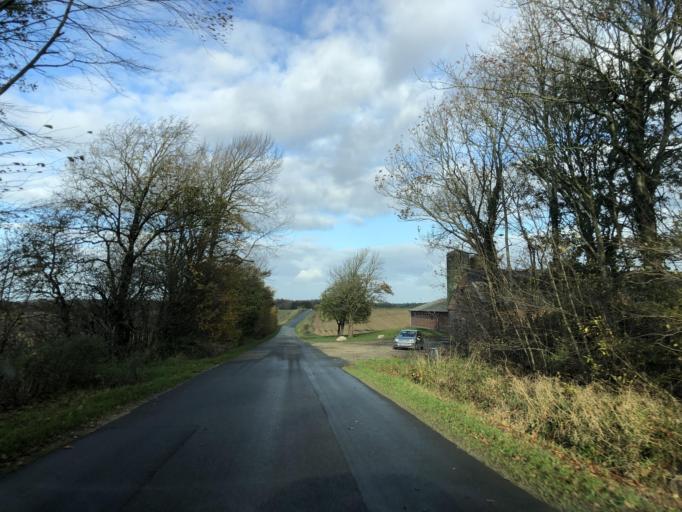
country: DK
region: Central Jutland
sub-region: Holstebro Kommune
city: Ulfborg
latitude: 56.1887
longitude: 8.4209
